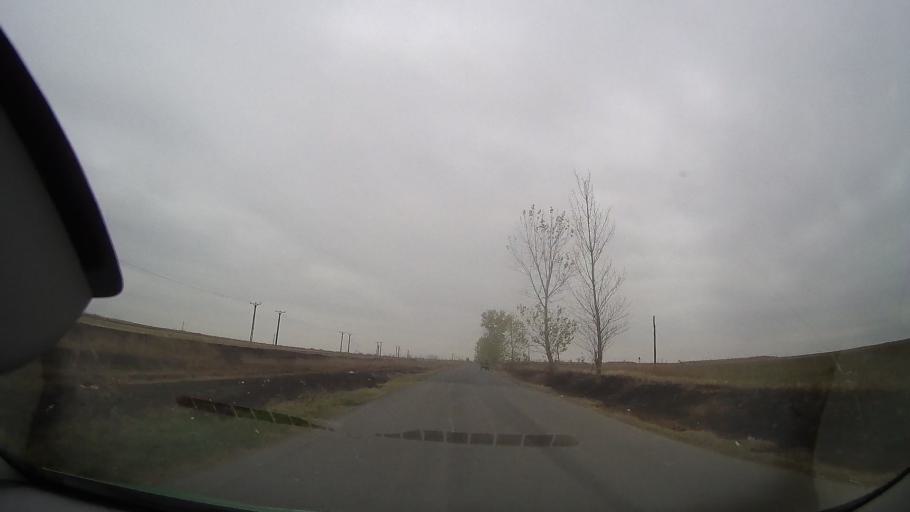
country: RO
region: Braila
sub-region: Comuna Ciocile
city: Ciocile
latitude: 44.8123
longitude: 27.2660
